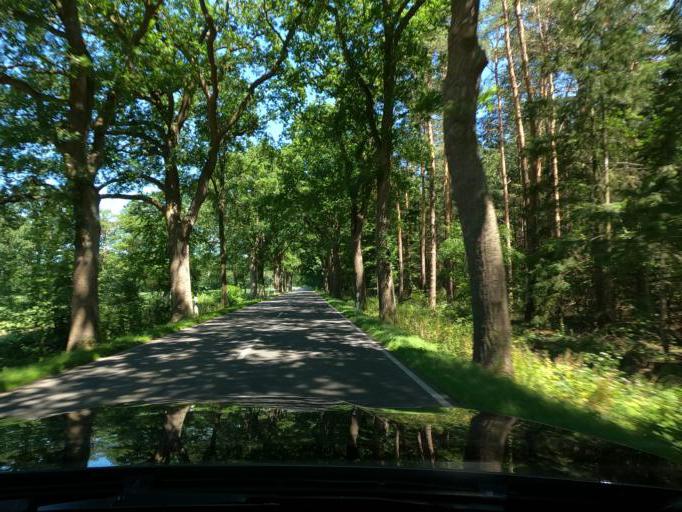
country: DE
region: Lower Saxony
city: Haenigsen
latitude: 52.5000
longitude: 10.1293
